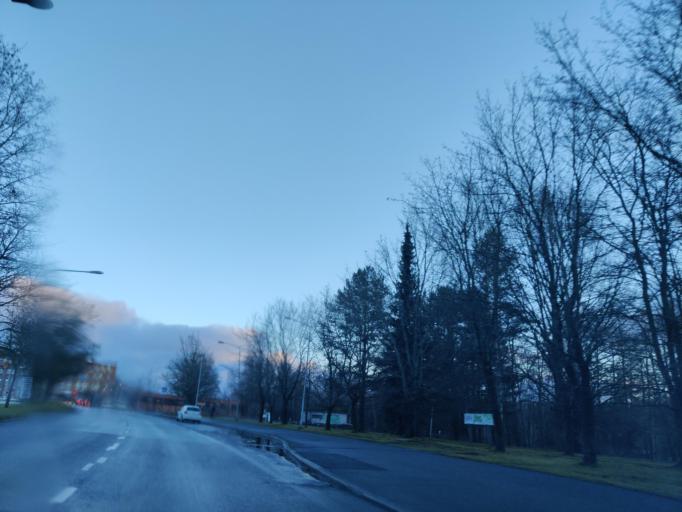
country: FI
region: Pirkanmaa
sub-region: Tampere
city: Nokia
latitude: 61.4752
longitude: 23.5022
